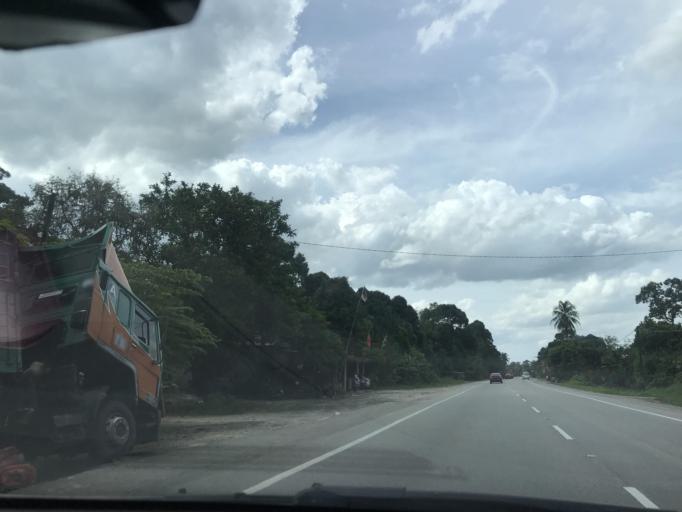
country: MY
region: Kelantan
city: Kampong Pangkal Kalong
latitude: 5.9024
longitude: 102.1862
